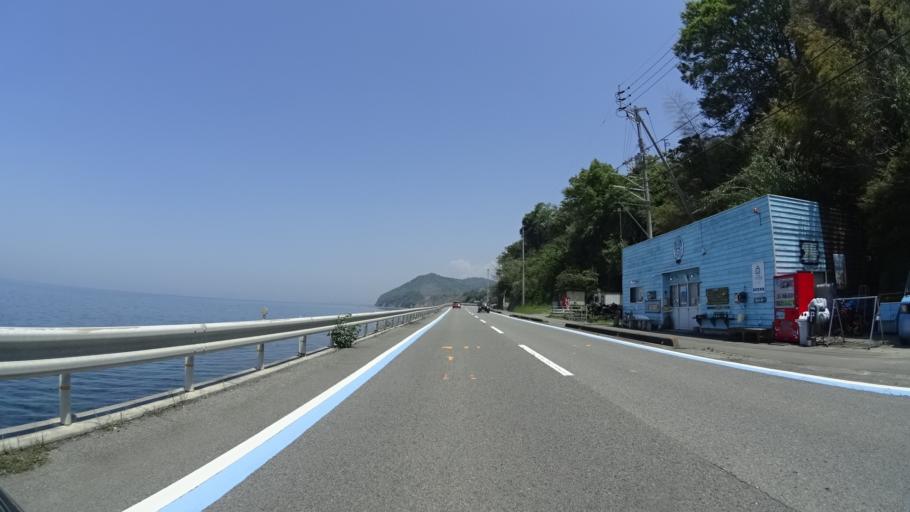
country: JP
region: Ehime
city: Iyo
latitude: 33.7009
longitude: 132.6564
